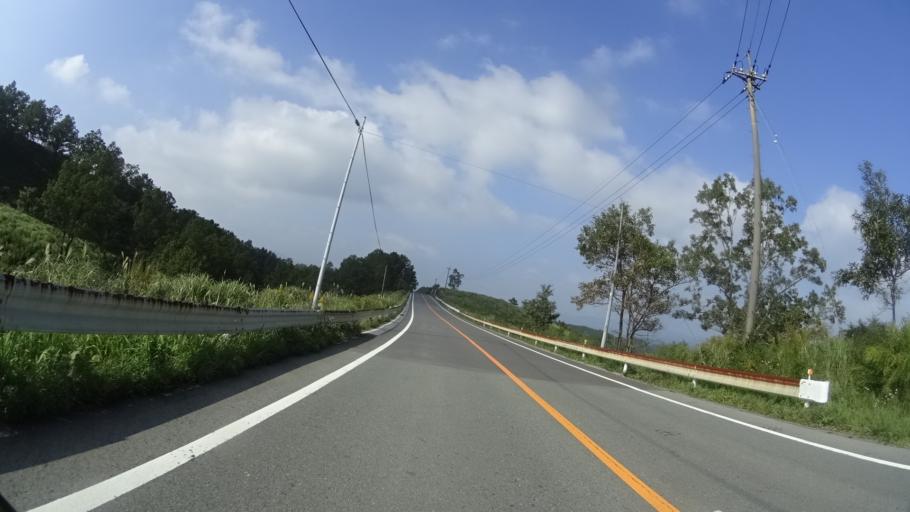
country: JP
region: Kumamoto
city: Aso
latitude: 33.0418
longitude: 131.0691
